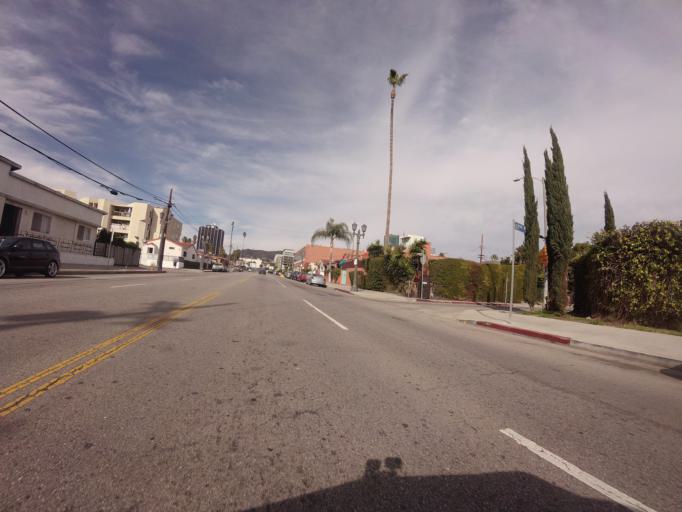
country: US
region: California
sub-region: Los Angeles County
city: Hollywood
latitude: 34.0931
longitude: -118.3289
